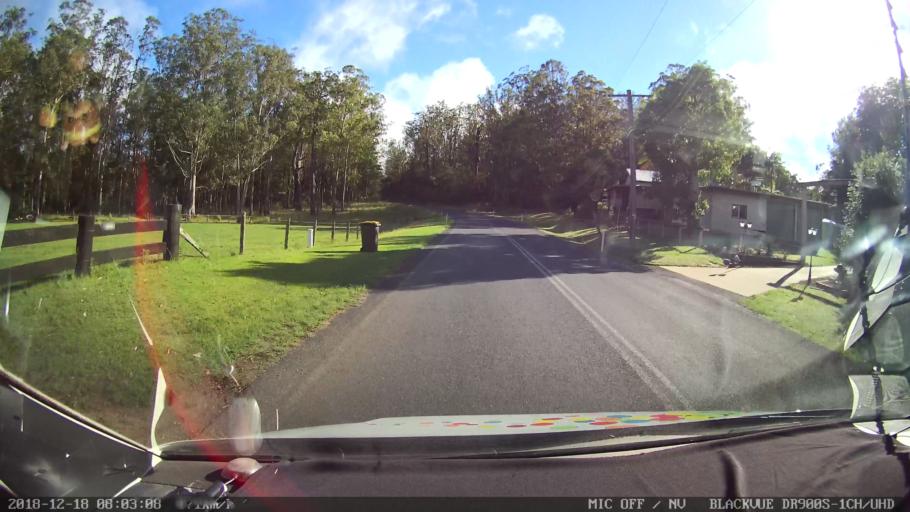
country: AU
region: New South Wales
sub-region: Kyogle
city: Kyogle
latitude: -28.3877
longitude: 152.6382
